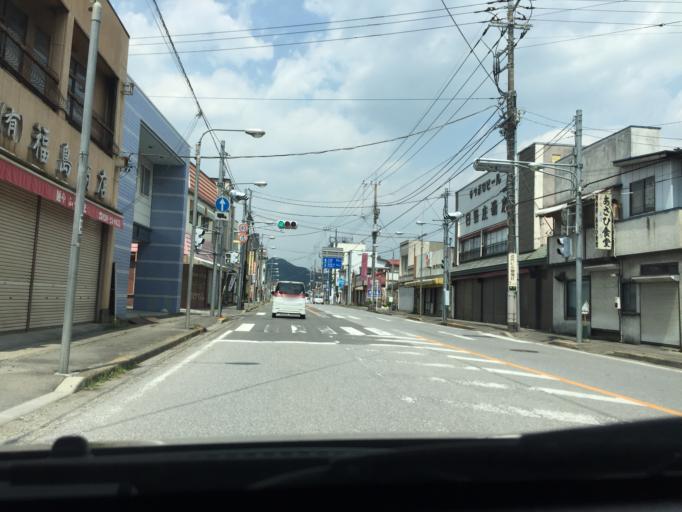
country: JP
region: Tochigi
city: Imaichi
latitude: 36.7273
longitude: 139.6860
